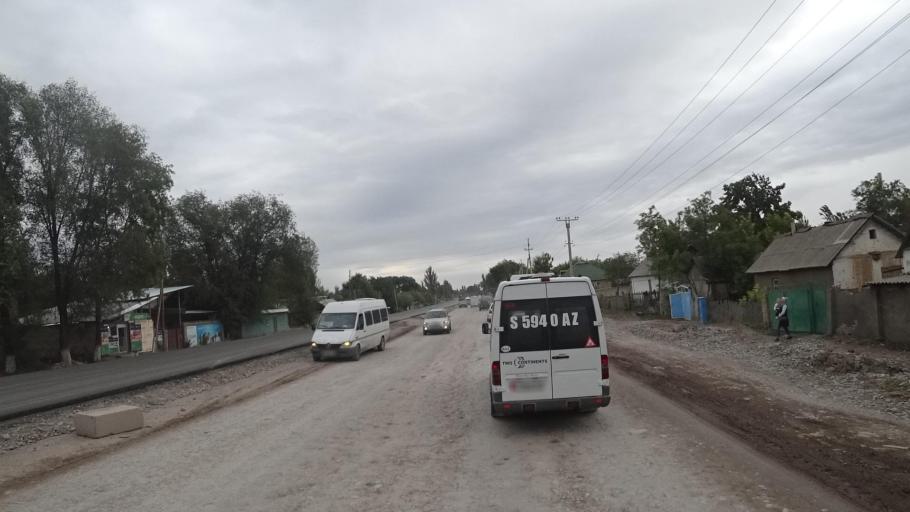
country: KG
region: Chuy
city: Belovodskoye
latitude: 42.8378
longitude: 74.1384
